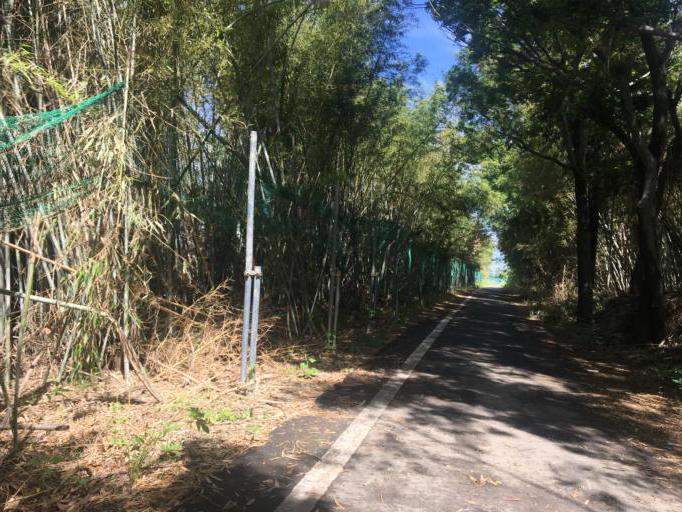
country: JP
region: Saitama
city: Shiki
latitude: 35.8644
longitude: 139.5842
